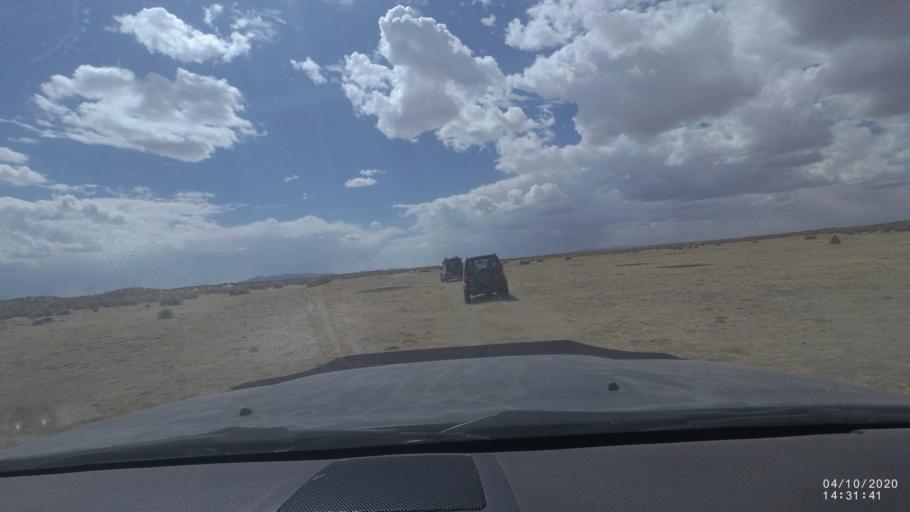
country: BO
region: Oruro
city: Poopo
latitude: -18.6744
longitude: -67.4634
